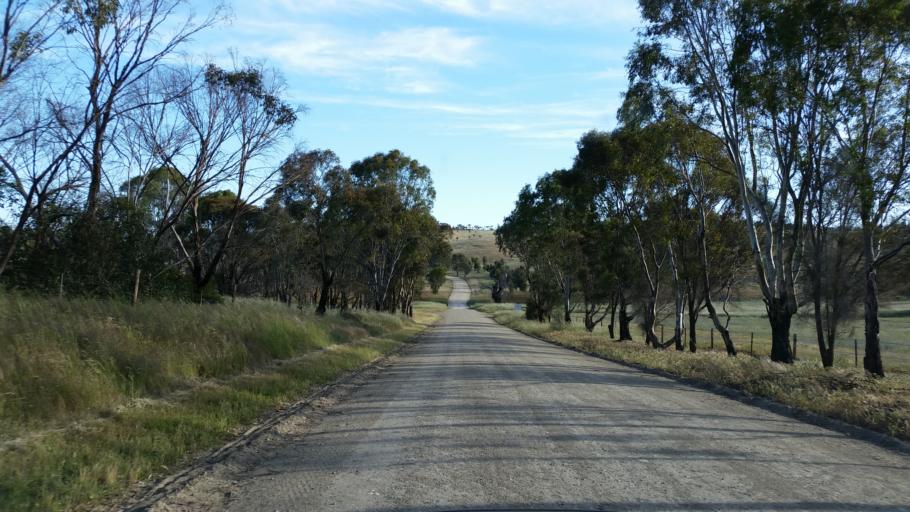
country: AU
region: South Australia
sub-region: Barossa
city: Angaston
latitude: -34.7005
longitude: 139.1688
